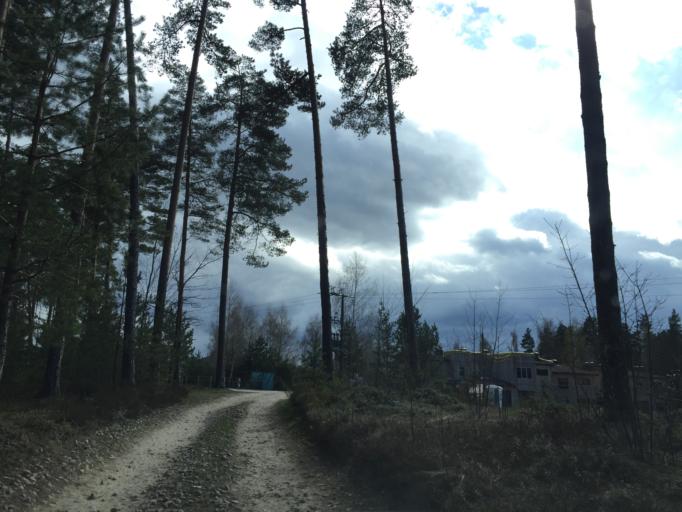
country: LV
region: Riga
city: Bergi
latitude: 56.9971
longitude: 24.2971
